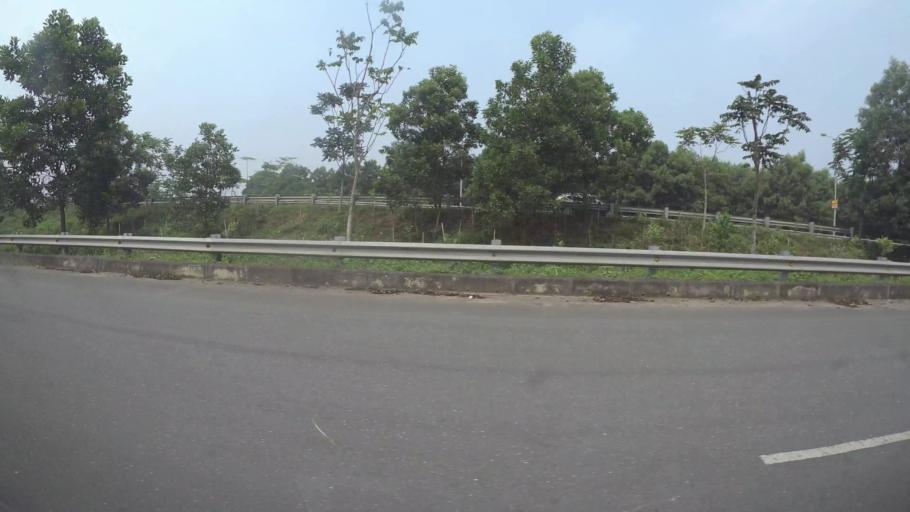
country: VN
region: Ha Noi
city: Lien Quan
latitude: 20.9921
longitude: 105.5276
